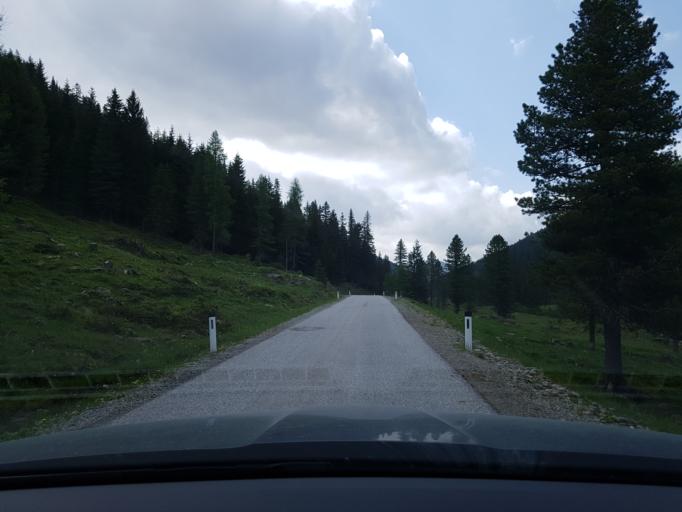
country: AT
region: Salzburg
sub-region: Politischer Bezirk Tamsweg
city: Thomatal
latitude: 47.0254
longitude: 13.7621
